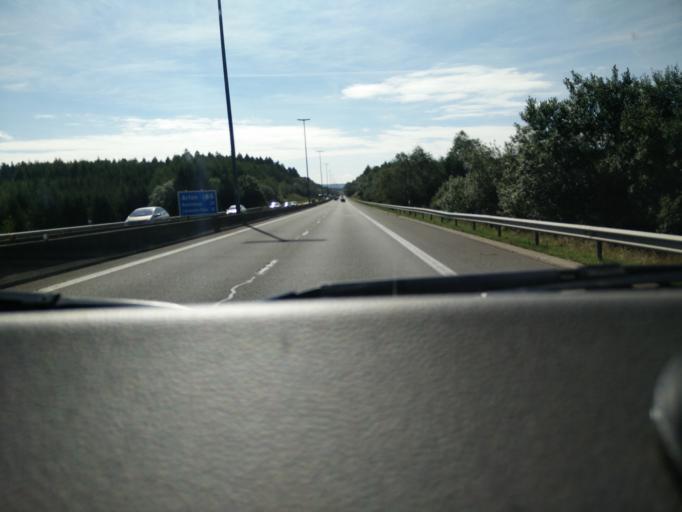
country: BE
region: Wallonia
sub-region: Province du Luxembourg
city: Libin
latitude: 49.9994
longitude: 5.2246
